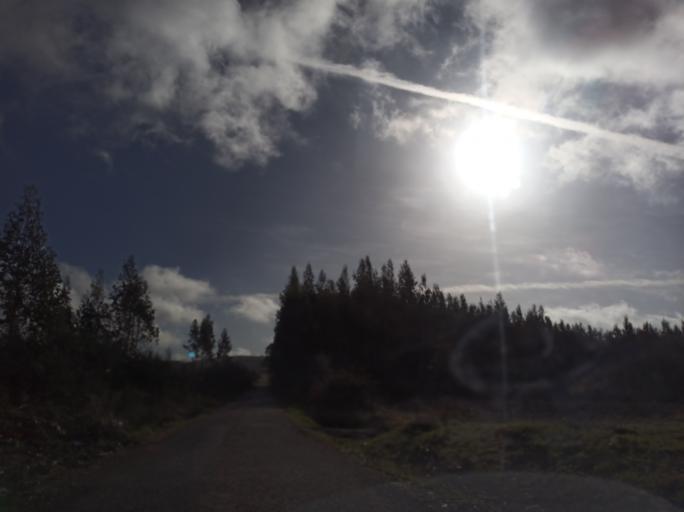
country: ES
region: Galicia
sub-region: Provincia da Coruna
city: Sobrado
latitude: 43.0813
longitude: -7.9595
